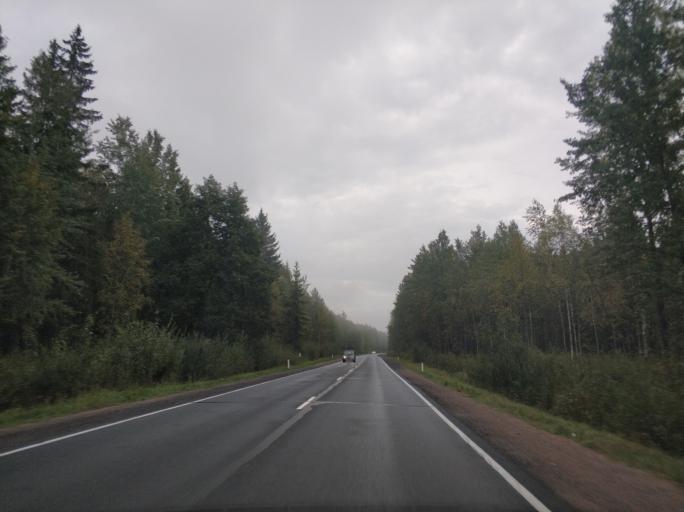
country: RU
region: Leningrad
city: Shcheglovo
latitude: 60.1012
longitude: 30.8282
